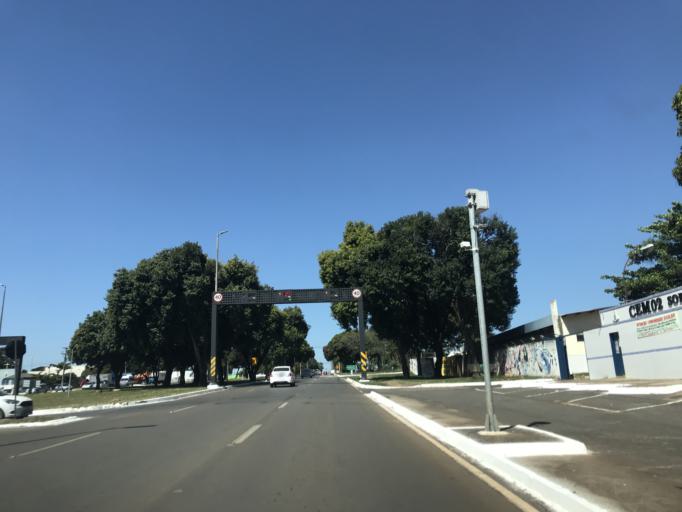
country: BR
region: Federal District
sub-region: Brasilia
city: Brasilia
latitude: -15.6479
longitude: -47.7862
